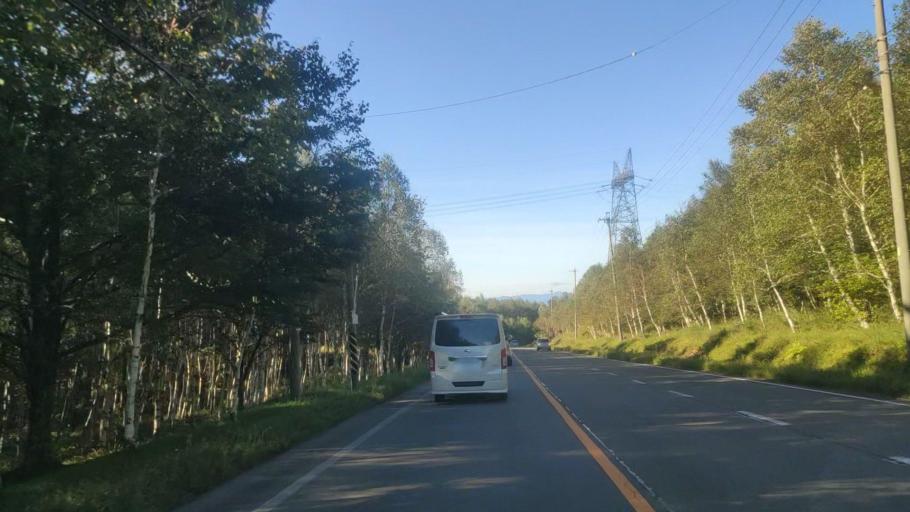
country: JP
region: Nagano
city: Kamimaruko
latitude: 36.1573
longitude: 138.2790
